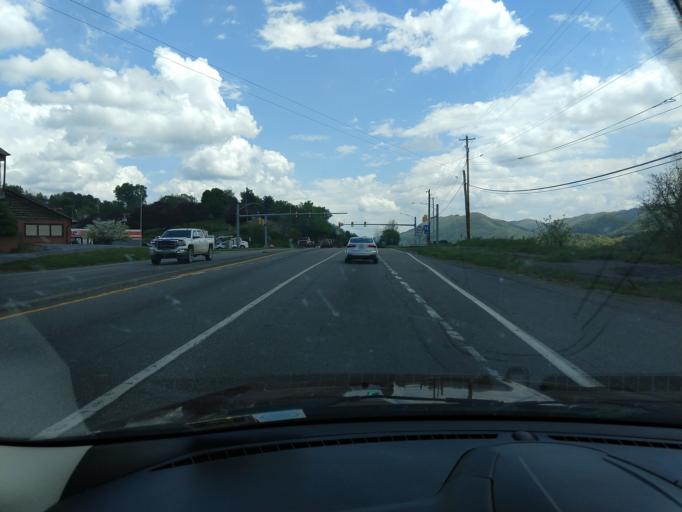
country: US
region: Virginia
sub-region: Tazewell County
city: Claypool Hill
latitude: 37.0616
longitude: -81.7537
